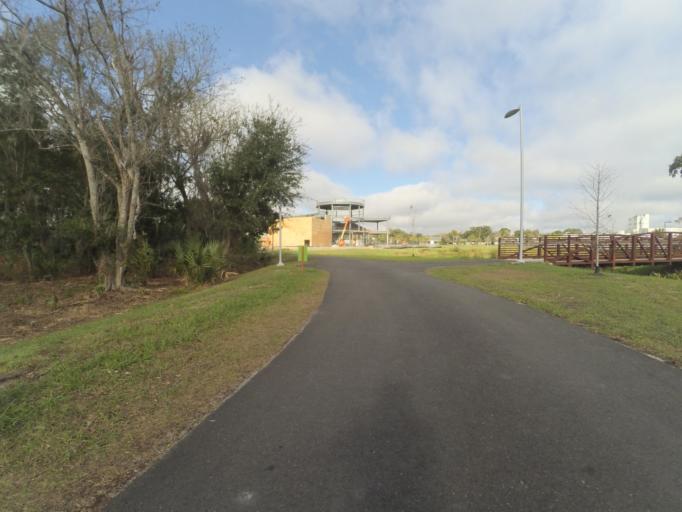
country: US
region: Florida
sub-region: Alachua County
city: Gainesville
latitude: 29.6425
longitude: -82.3243
